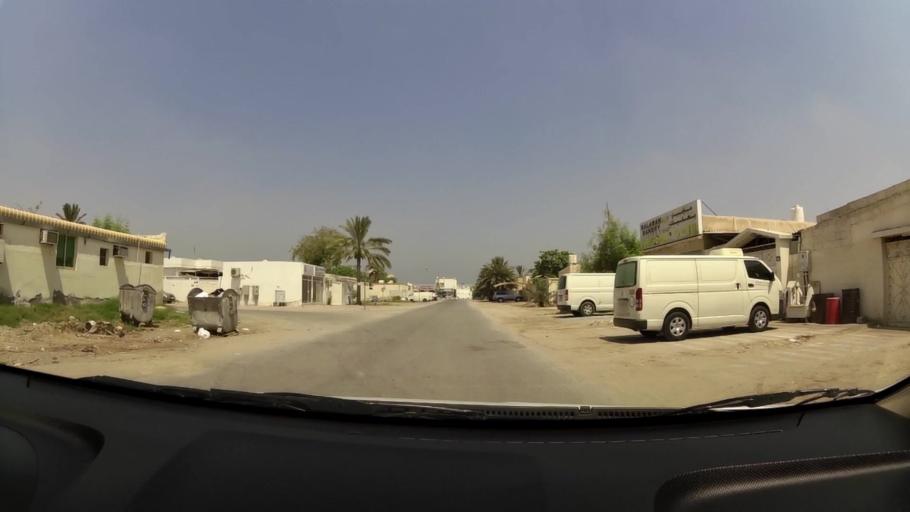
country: AE
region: Umm al Qaywayn
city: Umm al Qaywayn
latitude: 25.5606
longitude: 55.5563
